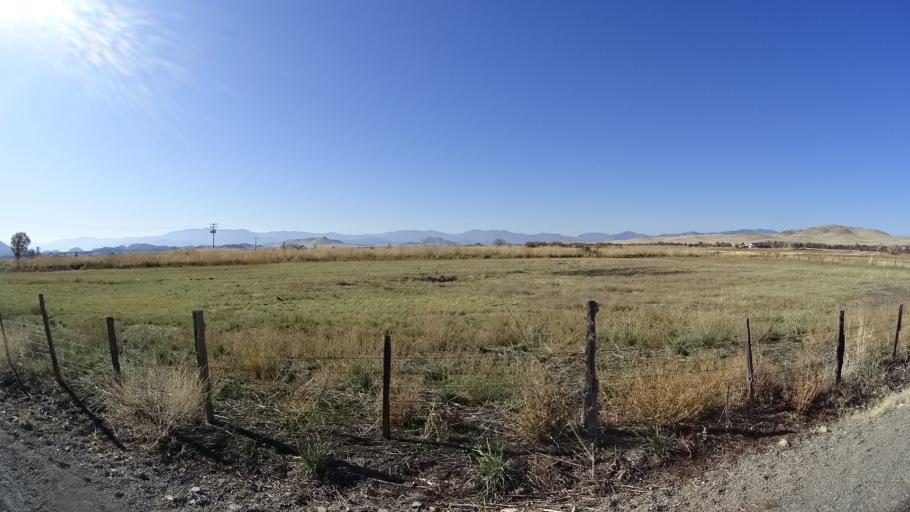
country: US
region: California
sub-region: Siskiyou County
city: Montague
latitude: 41.7183
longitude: -122.3893
